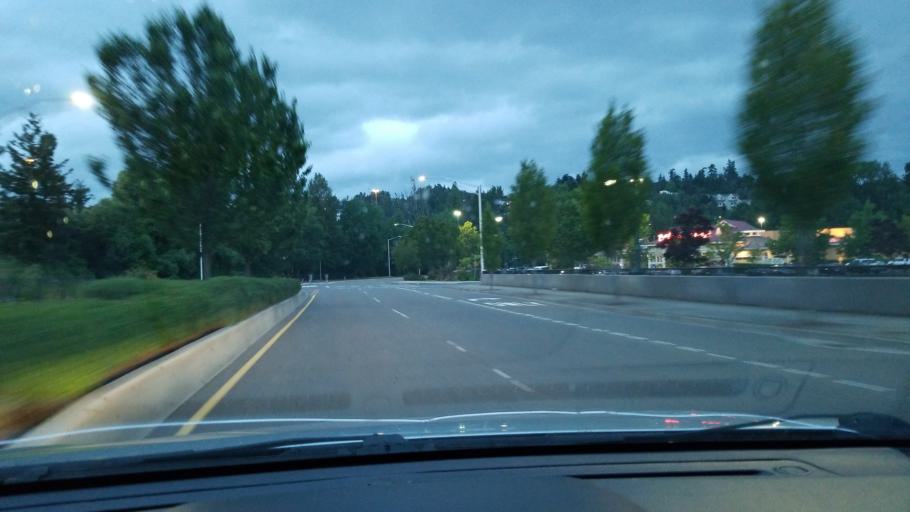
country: US
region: Washington
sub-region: King County
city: Tukwila
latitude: 47.4600
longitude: -122.2625
